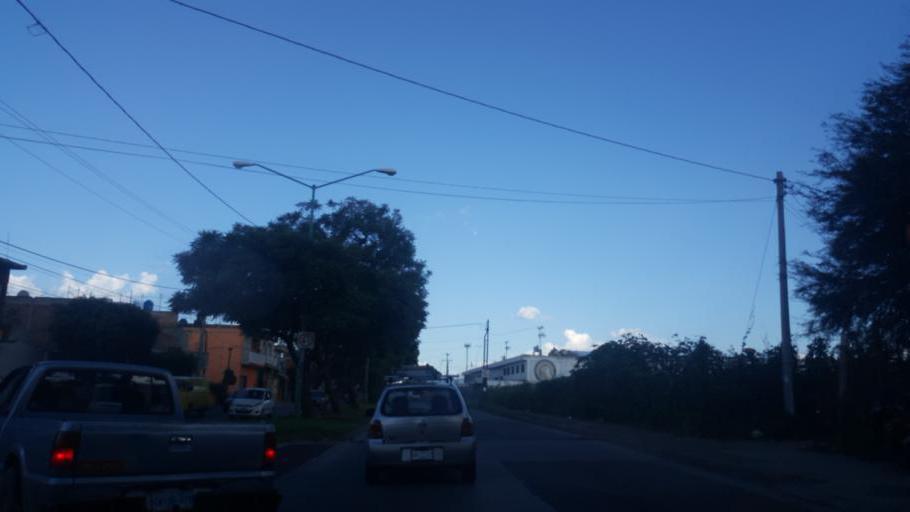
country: MX
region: Guanajuato
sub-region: Leon
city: San Jose de Duran (Los Troncoso)
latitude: 21.0923
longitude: -101.6833
